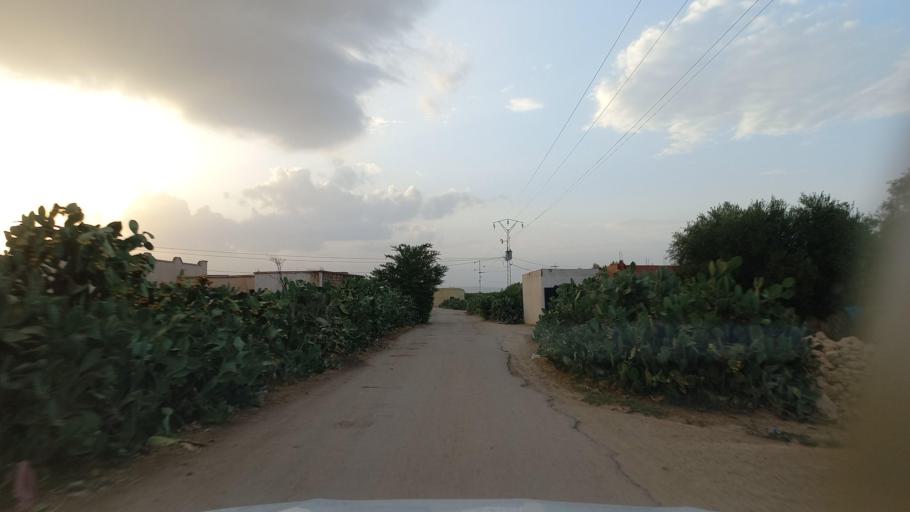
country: TN
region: Al Qasrayn
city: Kasserine
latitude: 35.2707
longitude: 9.0563
